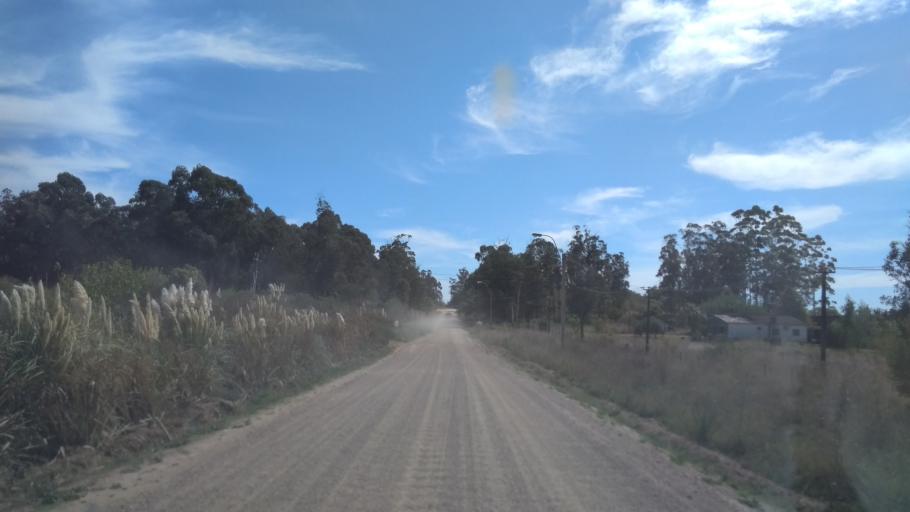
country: UY
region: Canelones
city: Joaquin Suarez
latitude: -34.7052
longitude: -56.0226
